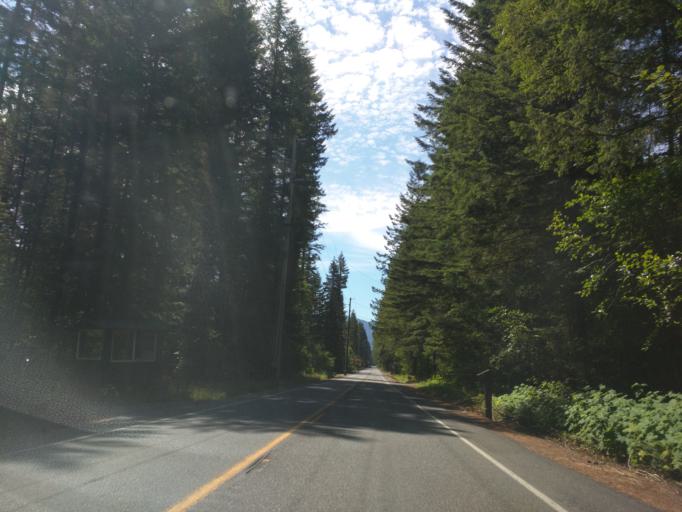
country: US
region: Washington
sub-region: Whatcom County
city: Peaceful Valley
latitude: 48.9559
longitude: -122.1568
